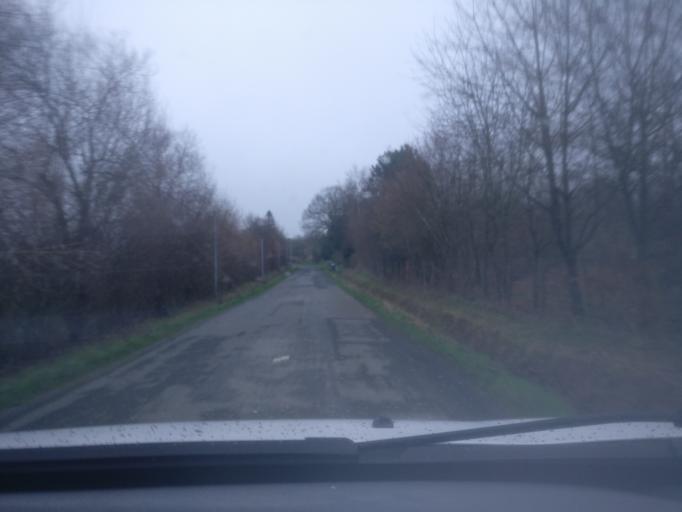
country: FR
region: Brittany
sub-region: Departement d'Ille-et-Vilaine
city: Saint-Medard-sur-Ille
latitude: 48.2947
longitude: -1.6068
